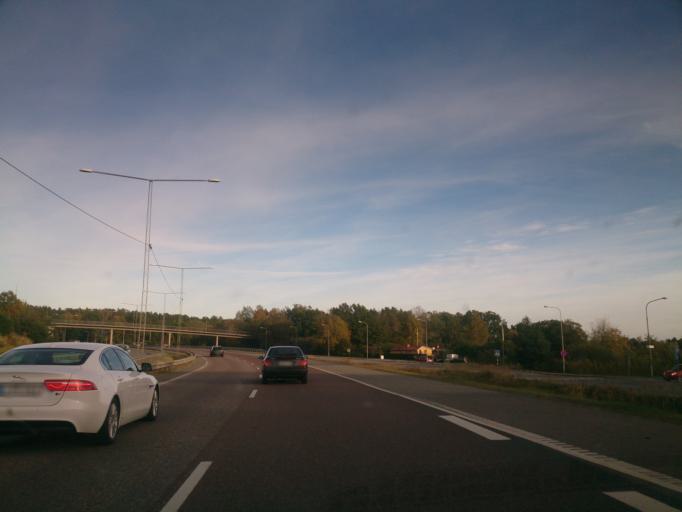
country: SE
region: Stockholm
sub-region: Nacka Kommun
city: Alta
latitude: 59.2620
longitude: 18.1312
